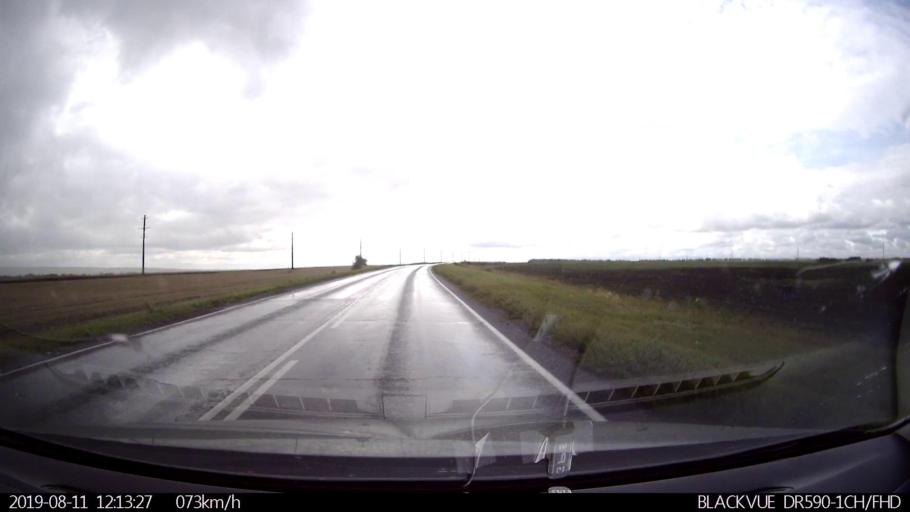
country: RU
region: Ulyanovsk
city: Silikatnyy
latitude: 53.9617
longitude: 47.9919
